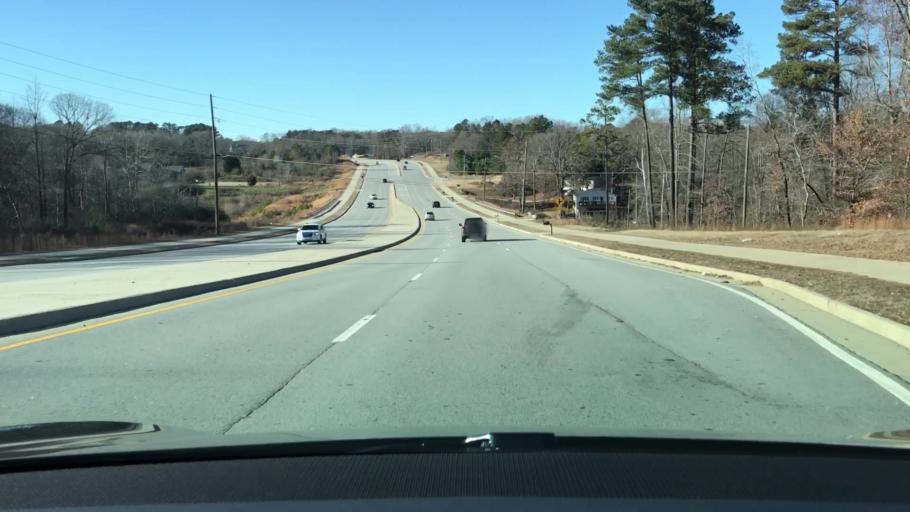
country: US
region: Georgia
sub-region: Hall County
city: Flowery Branch
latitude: 34.1111
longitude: -83.8911
